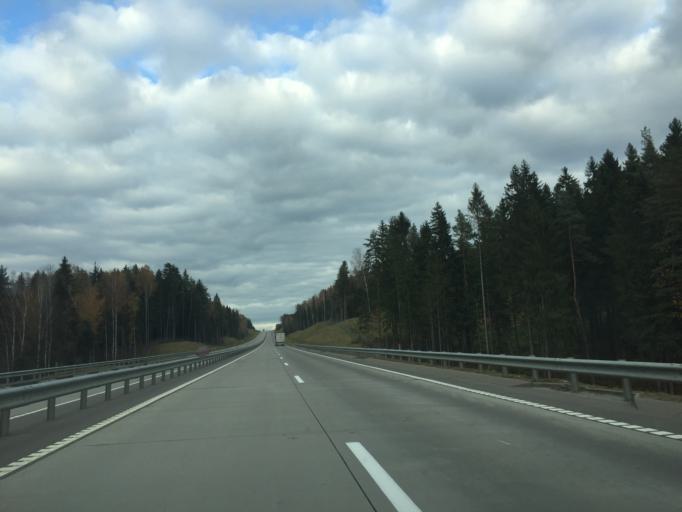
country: BY
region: Minsk
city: Rakaw
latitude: 53.9873
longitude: 27.1069
